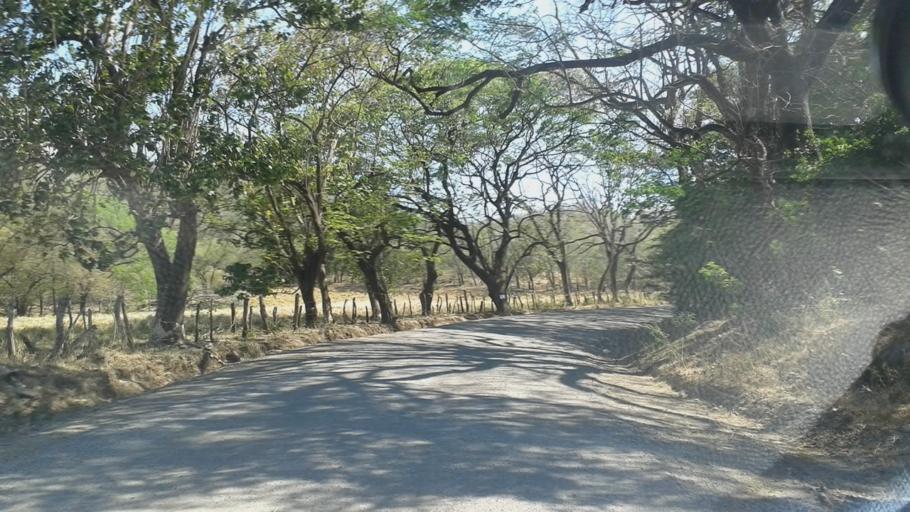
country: CR
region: Guanacaste
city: Santa Cruz
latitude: 10.1926
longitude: -85.7589
